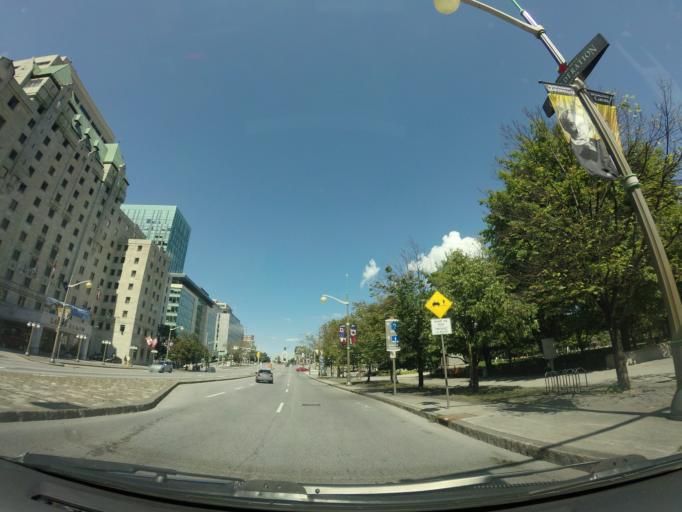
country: CA
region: Ontario
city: Ottawa
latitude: 45.4213
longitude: -75.6930
